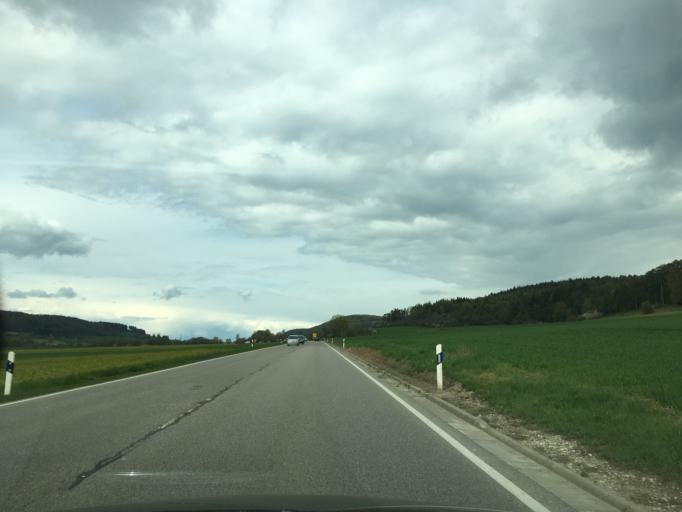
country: DE
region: Bavaria
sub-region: Regierungsbezirk Mittelfranken
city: Treuchtlingen
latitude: 48.9513
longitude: 10.9369
